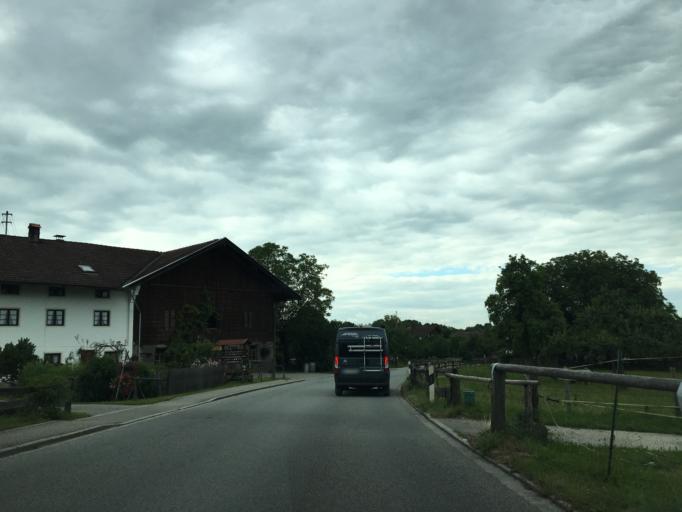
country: DE
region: Bavaria
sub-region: Upper Bavaria
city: Bad Feilnbach
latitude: 47.7737
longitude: 12.0131
